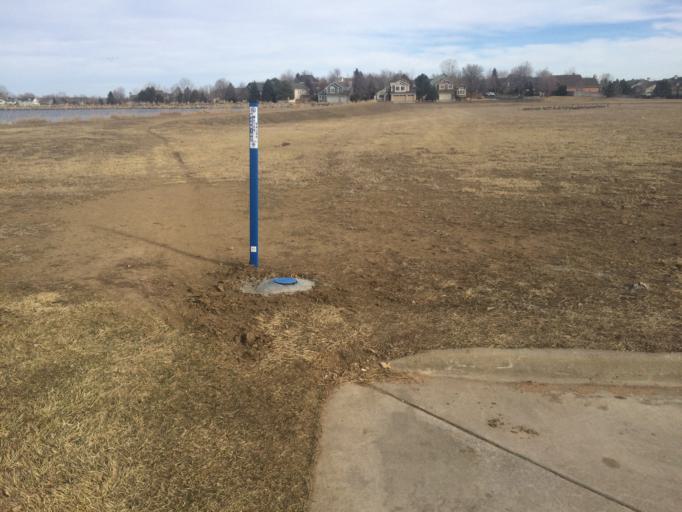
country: US
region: Colorado
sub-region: Broomfield County
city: Broomfield
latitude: 39.9187
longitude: -105.0648
